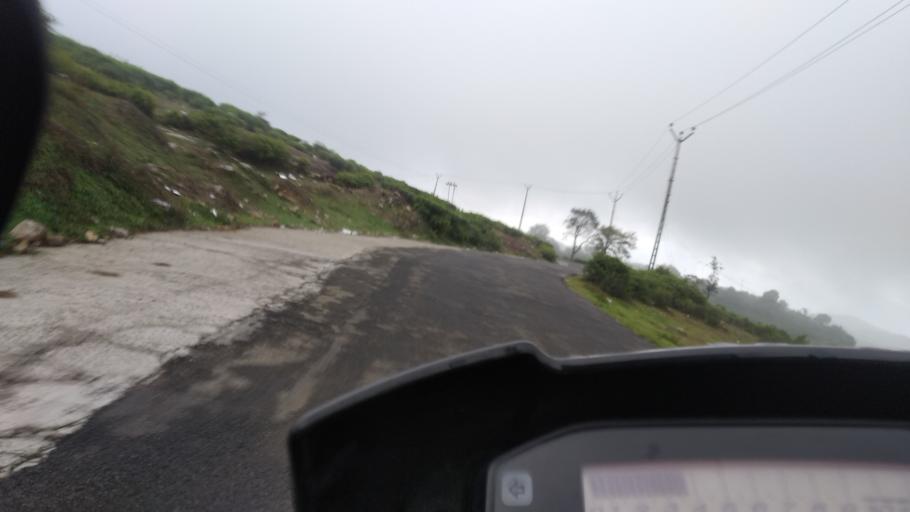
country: IN
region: Kerala
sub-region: Kottayam
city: Erattupetta
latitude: 9.6307
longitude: 76.9396
